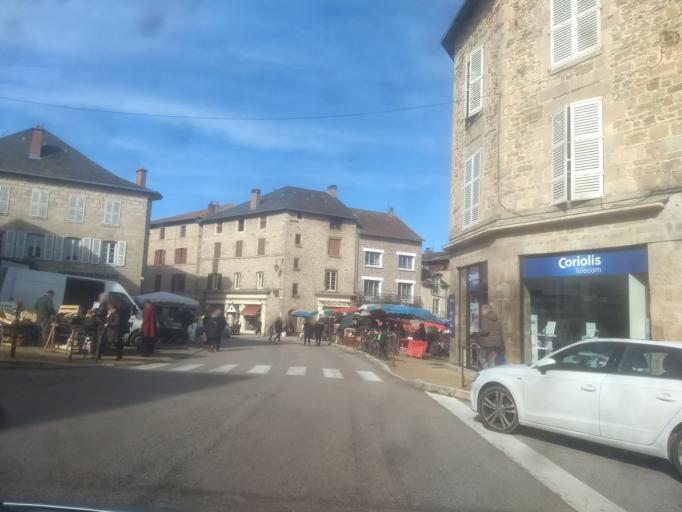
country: FR
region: Limousin
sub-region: Departement de la Haute-Vienne
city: Eymoutiers
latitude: 45.7387
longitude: 1.7436
